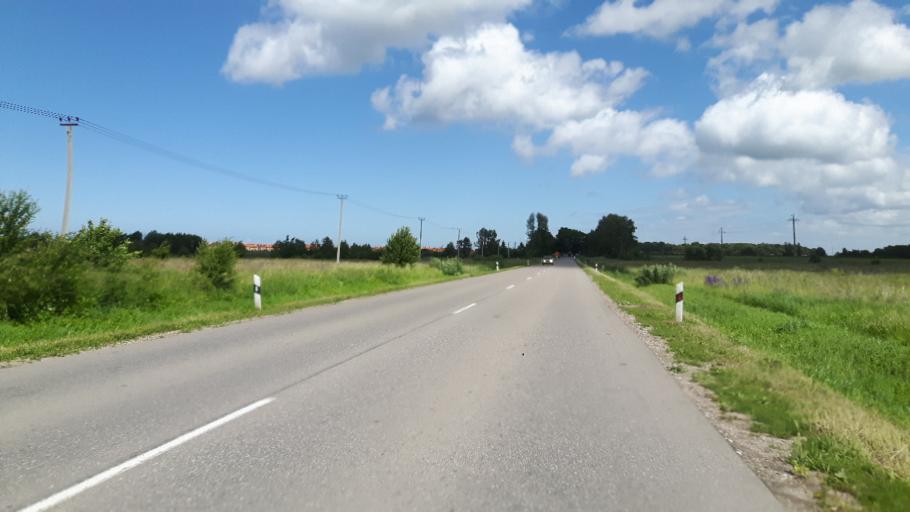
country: RU
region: Kaliningrad
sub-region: Zelenogradskiy Rayon
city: Zelenogradsk
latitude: 54.9325
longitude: 20.4329
